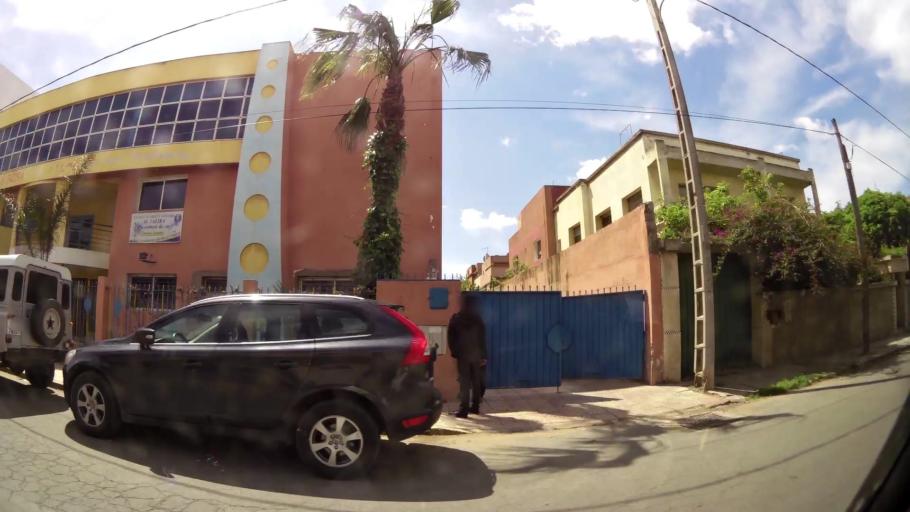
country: MA
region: Grand Casablanca
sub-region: Mediouna
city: Tit Mellil
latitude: 33.6097
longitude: -7.5315
